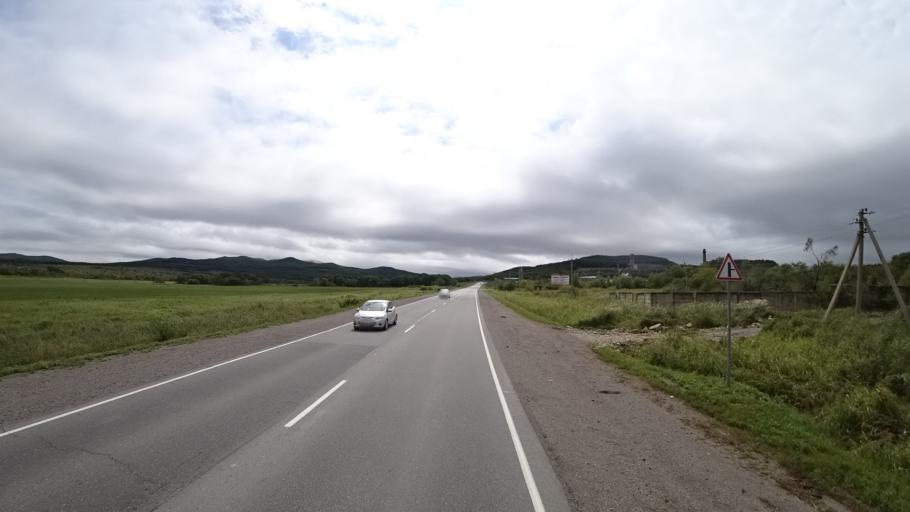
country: RU
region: Primorskiy
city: Monastyrishche
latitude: 44.1714
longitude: 132.4412
